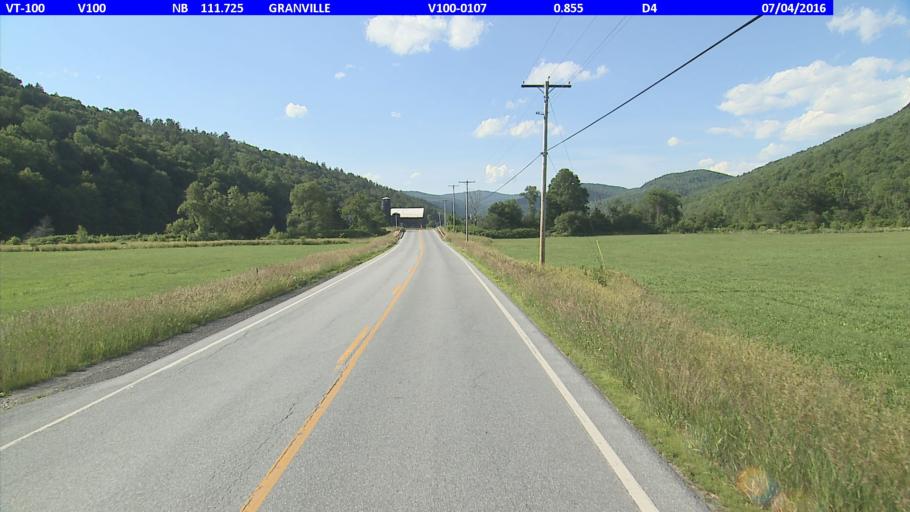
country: US
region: Vermont
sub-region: Orange County
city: Randolph
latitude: 43.9569
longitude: -72.8398
